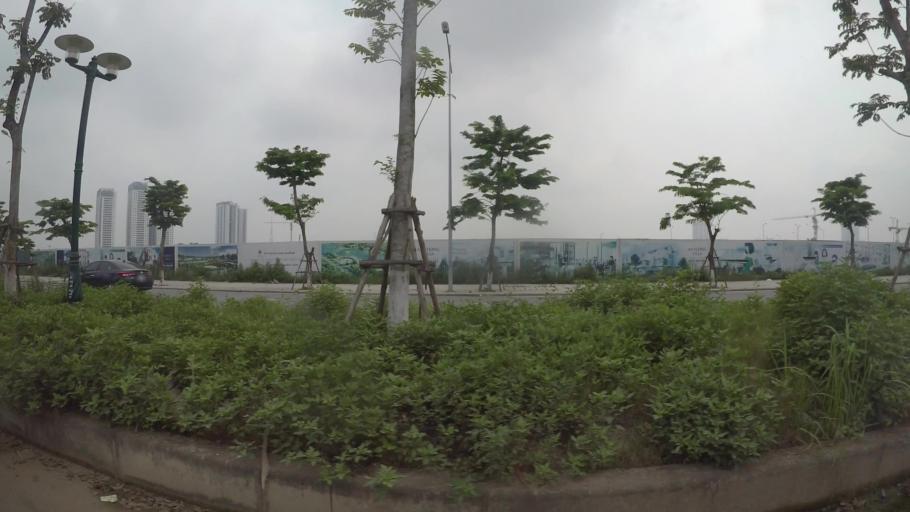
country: VN
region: Ha Noi
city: Ha Dong
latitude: 20.9850
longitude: 105.7544
